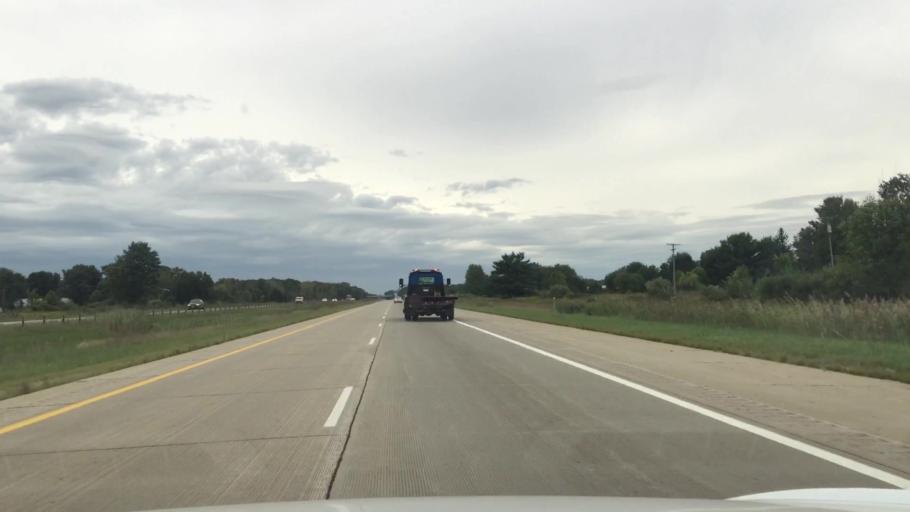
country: US
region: Michigan
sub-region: Saint Clair County
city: Saint Clair
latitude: 42.8482
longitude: -82.5782
